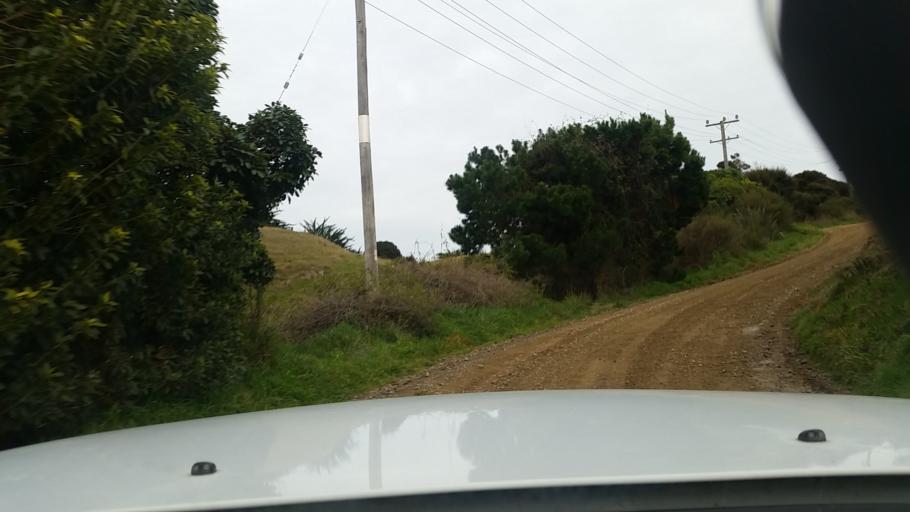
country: NZ
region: Canterbury
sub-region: Christchurch City
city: Christchurch
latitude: -43.6351
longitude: 172.7302
